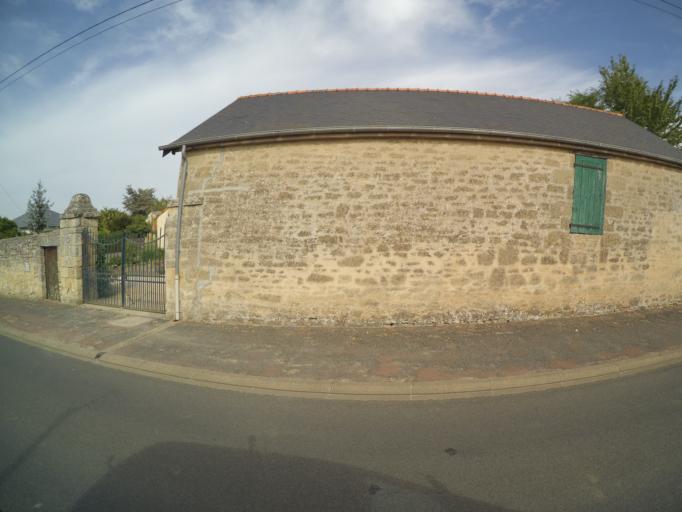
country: FR
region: Pays de la Loire
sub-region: Departement de Maine-et-Loire
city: Doue-la-Fontaine
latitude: 47.1934
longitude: -0.2931
